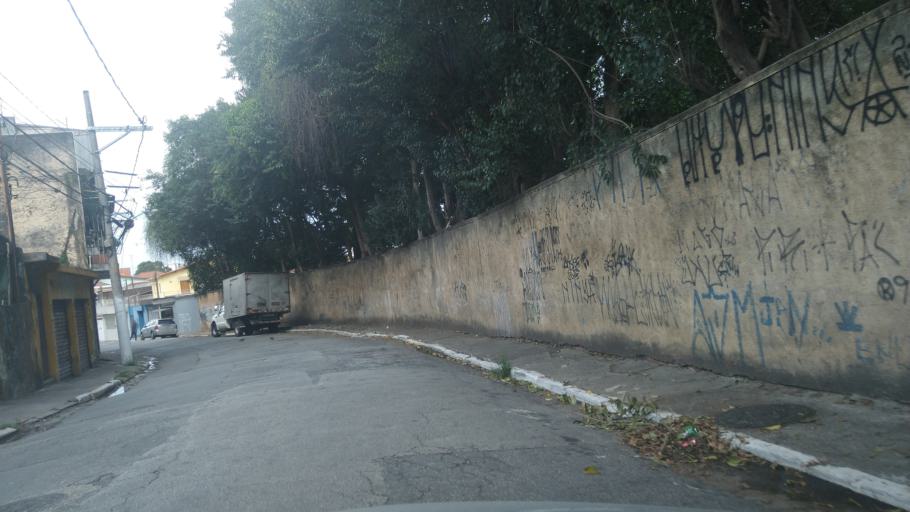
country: BR
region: Sao Paulo
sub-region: Sao Paulo
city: Sao Paulo
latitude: -23.4852
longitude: -46.6401
